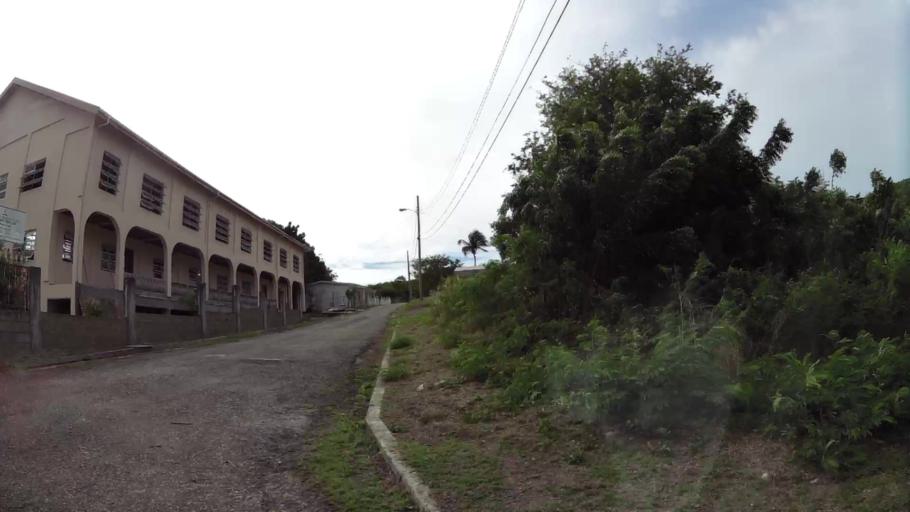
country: AG
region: Saint Peter
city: Parham
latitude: 17.0576
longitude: -61.7253
